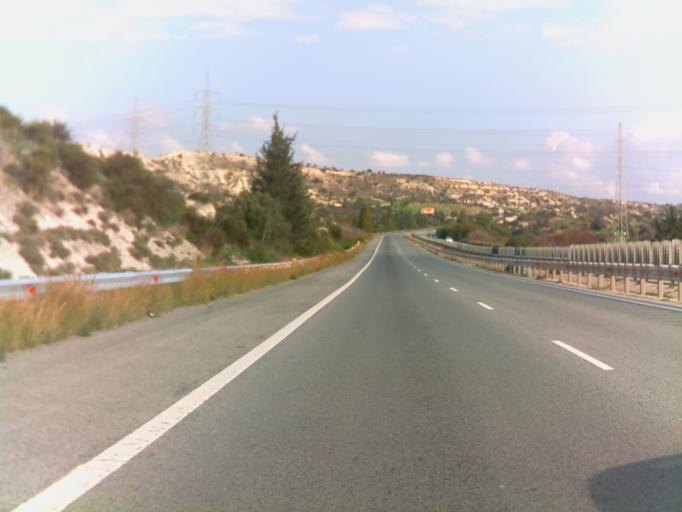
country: CY
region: Limassol
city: Pyrgos
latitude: 34.7361
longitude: 33.2840
